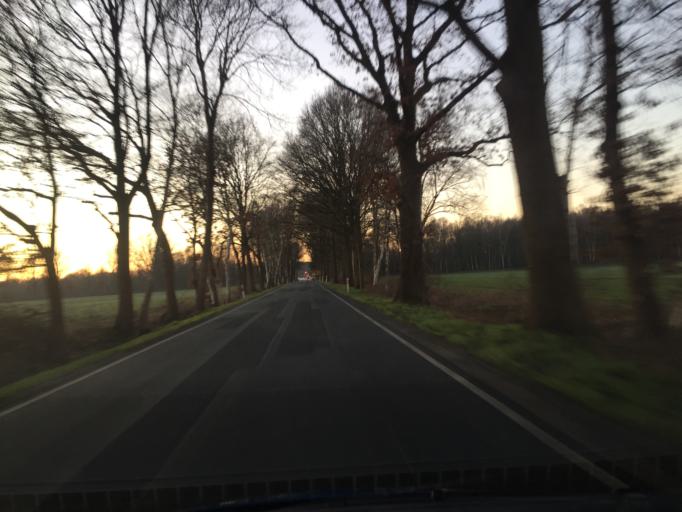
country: DE
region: Lower Saxony
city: Adelheidsdorf
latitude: 52.5234
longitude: 10.0379
